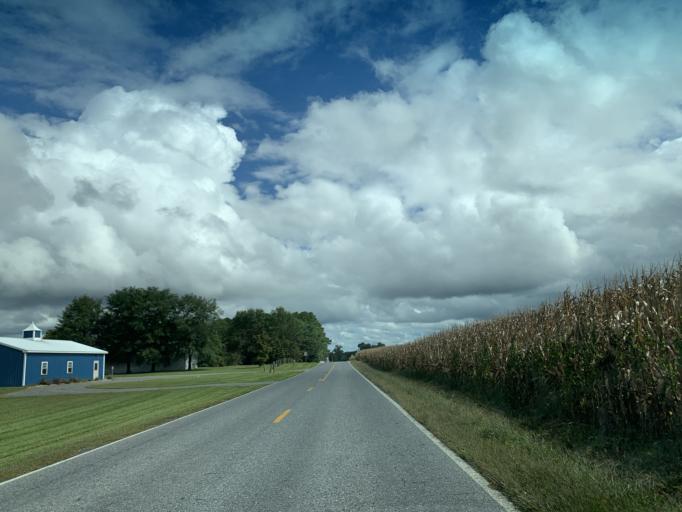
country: US
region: Maryland
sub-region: Caroline County
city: Denton
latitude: 38.9074
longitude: -75.8470
